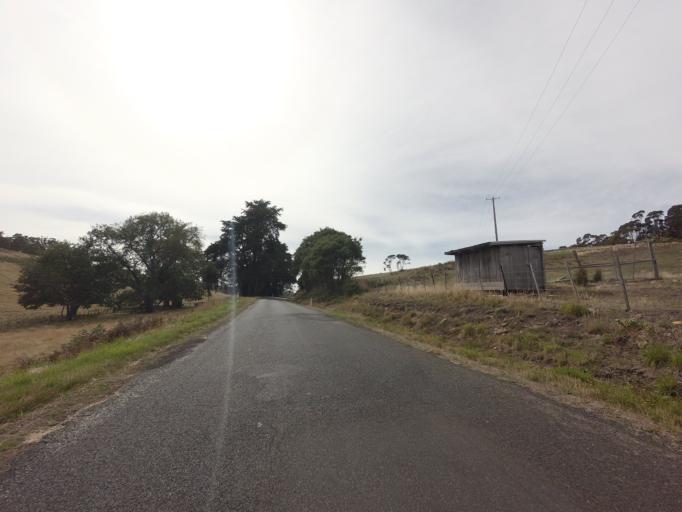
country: AU
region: Tasmania
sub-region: Sorell
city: Sorell
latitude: -42.4443
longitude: 147.5428
